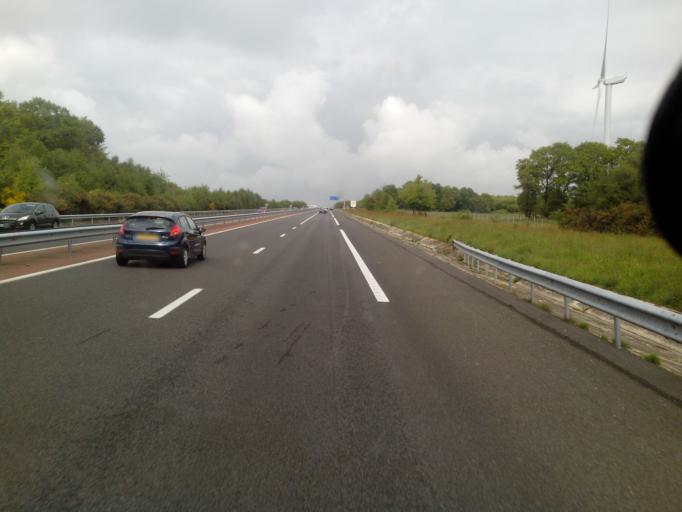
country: FR
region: Lower Normandy
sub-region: Departement de la Manche
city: Percy
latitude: 48.9025
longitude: -1.1108
